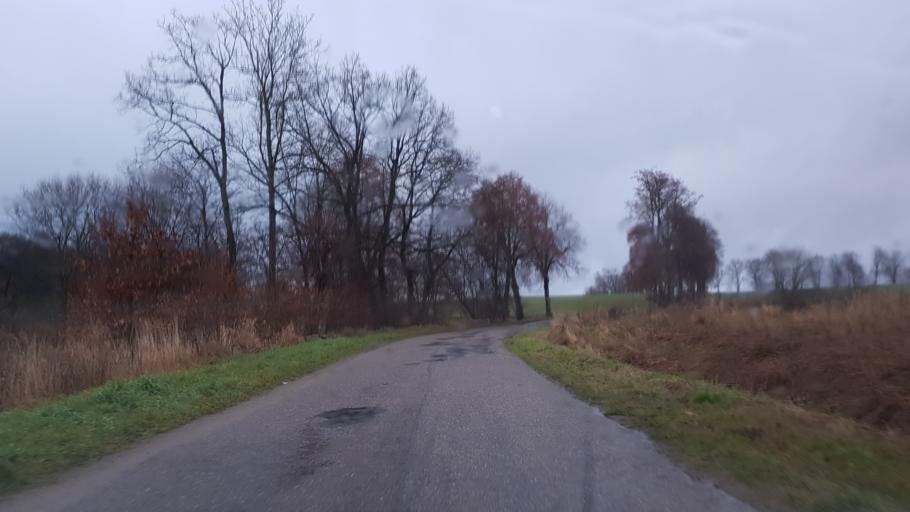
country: PL
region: West Pomeranian Voivodeship
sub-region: Powiat bialogardzki
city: Bialogard
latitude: 53.9376
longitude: 16.0065
